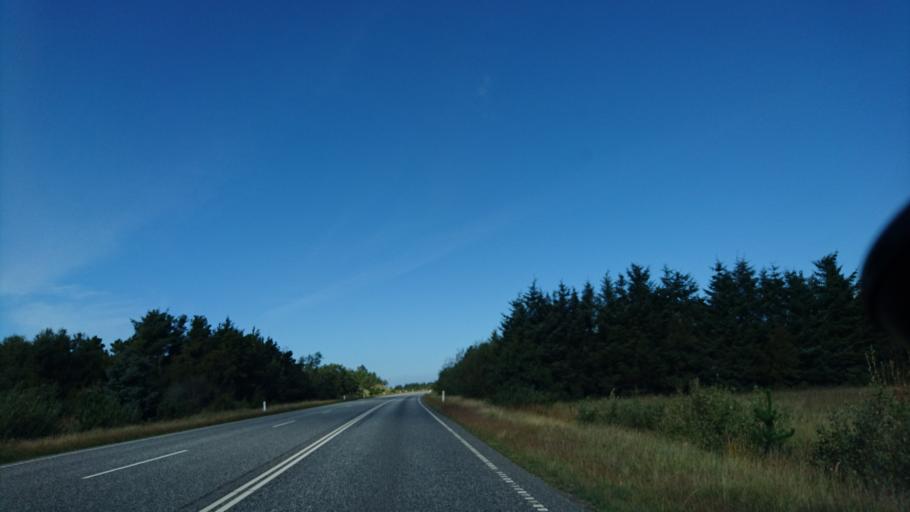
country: DK
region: North Denmark
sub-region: Frederikshavn Kommune
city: Skagen
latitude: 57.6633
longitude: 10.4554
